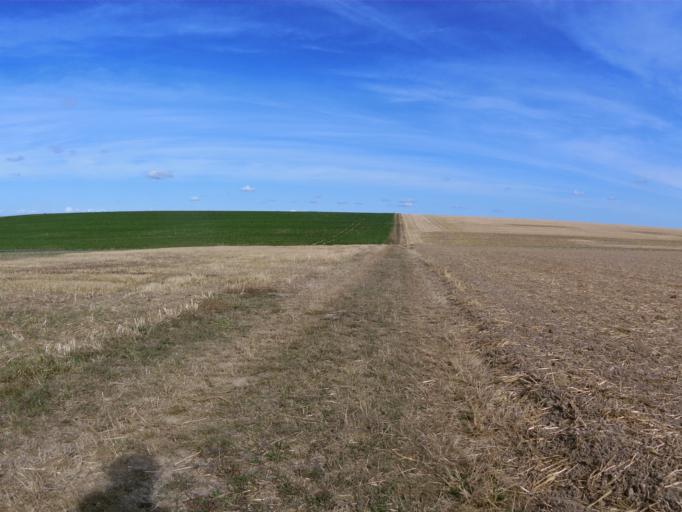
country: DE
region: Bavaria
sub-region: Regierungsbezirk Unterfranken
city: Rimpar
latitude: 49.8351
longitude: 9.9376
